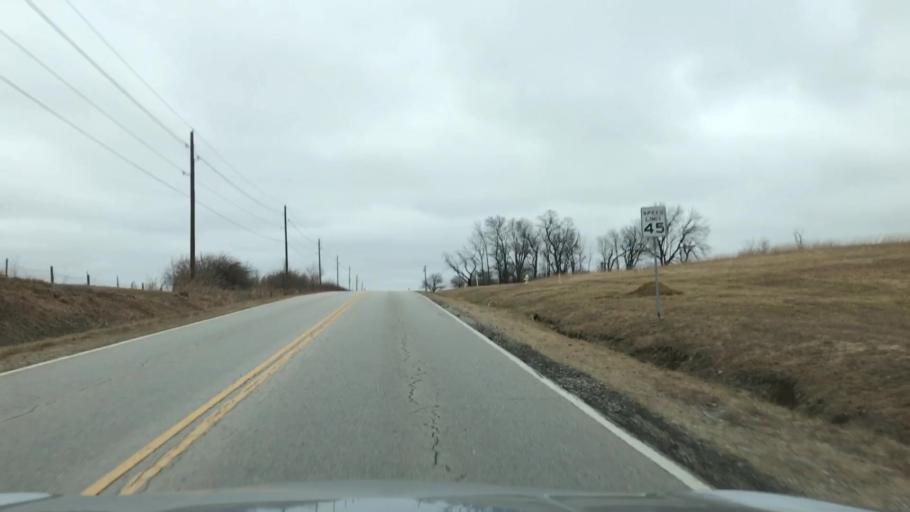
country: US
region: Missouri
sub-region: Clay County
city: Liberty
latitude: 39.2722
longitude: -94.4166
